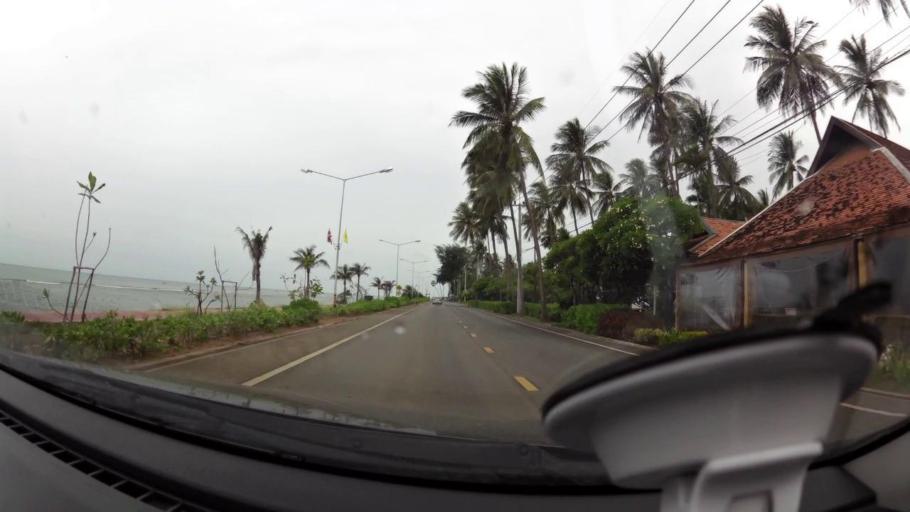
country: TH
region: Prachuap Khiri Khan
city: Pran Buri
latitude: 12.3858
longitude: 99.9989
